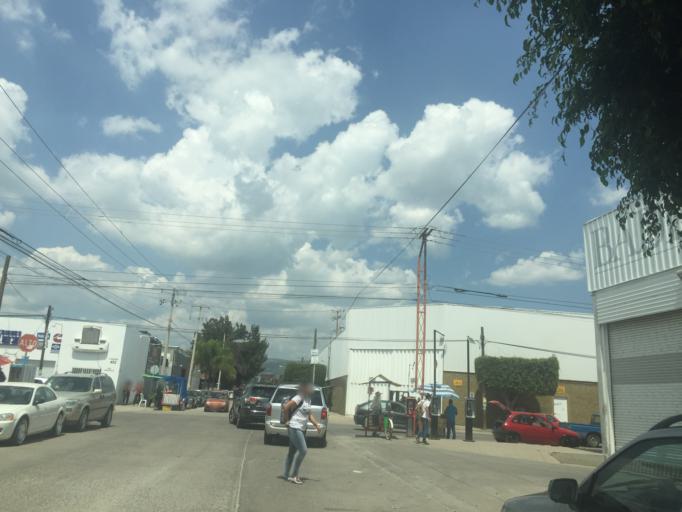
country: MX
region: Guanajuato
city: Leon
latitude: 21.1648
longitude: -101.6725
